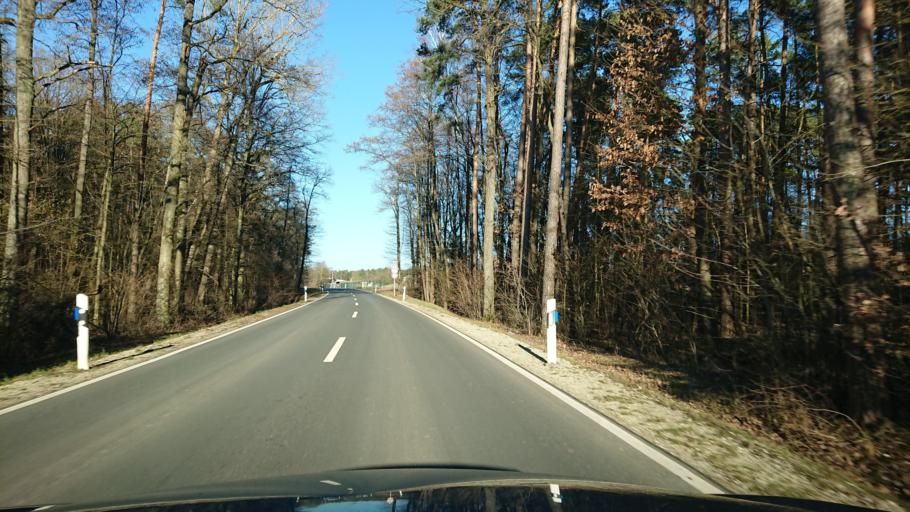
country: DE
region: Bavaria
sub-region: Upper Franconia
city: Pinzberg
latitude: 49.6894
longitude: 11.0809
